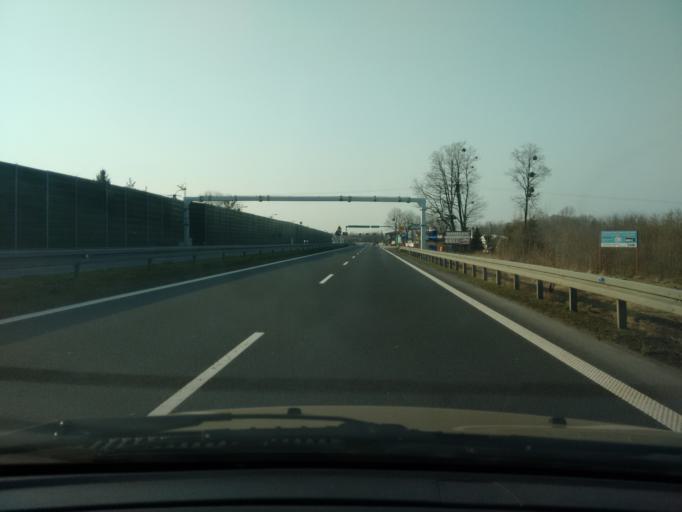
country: PL
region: Silesian Voivodeship
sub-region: Powiat cieszynski
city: Ochaby
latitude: 49.8401
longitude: 18.7710
